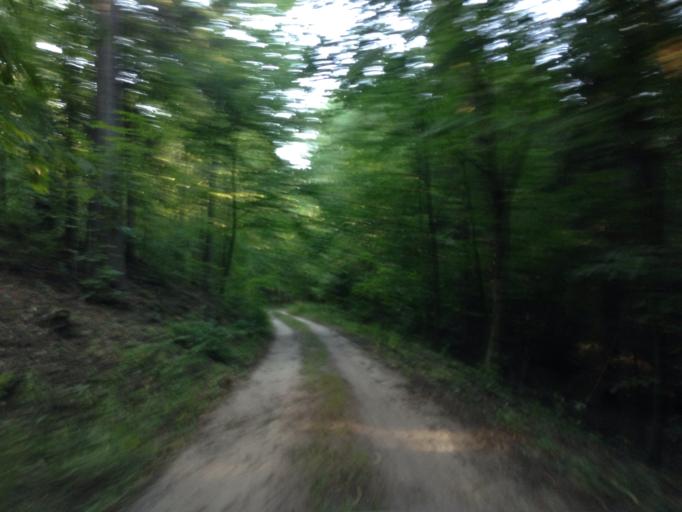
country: PL
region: Kujawsko-Pomorskie
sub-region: Powiat brodnicki
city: Gorzno
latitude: 53.2241
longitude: 19.7306
